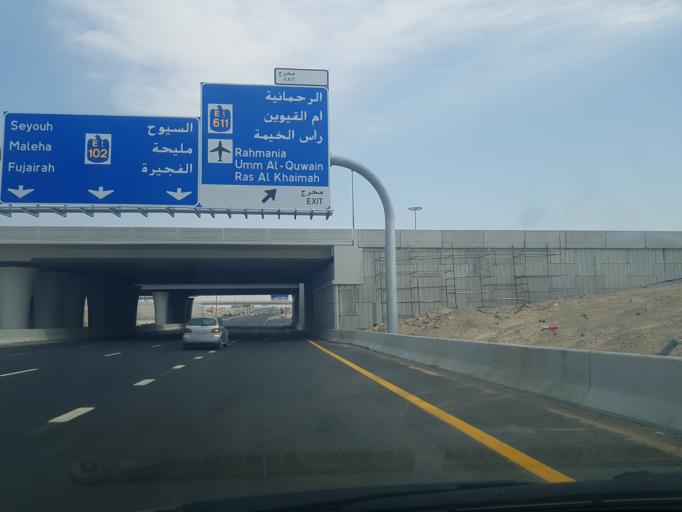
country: AE
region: Ash Shariqah
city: Sharjah
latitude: 25.2386
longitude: 55.5653
